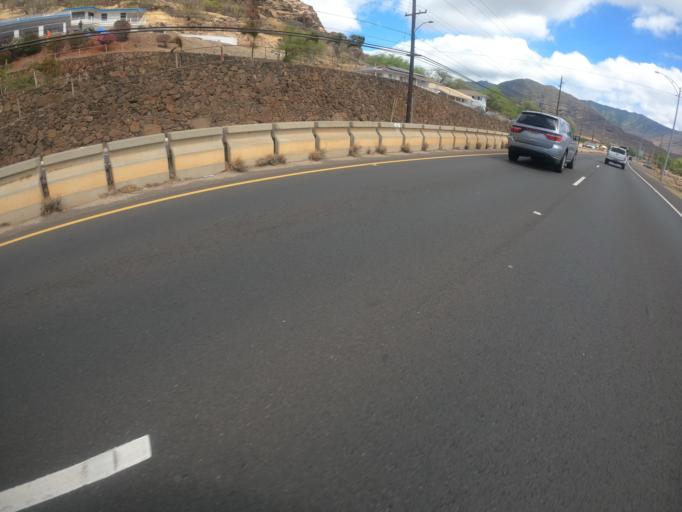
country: US
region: Hawaii
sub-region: Honolulu County
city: Nanakuli
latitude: 21.3970
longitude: -158.1670
